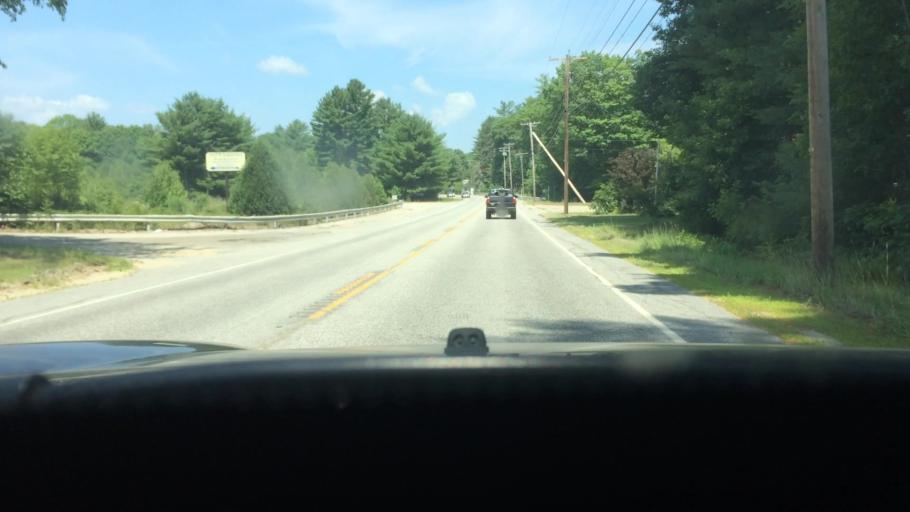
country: US
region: Maine
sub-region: Androscoggin County
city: Mechanic Falls
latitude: 44.1015
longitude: -70.3628
